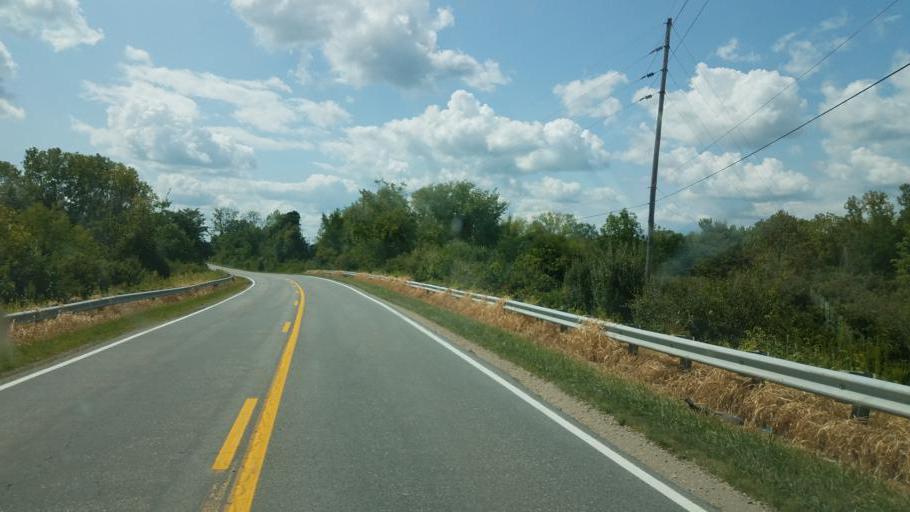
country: US
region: Ohio
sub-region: Delaware County
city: Lewis Center
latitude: 40.2395
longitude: -82.9810
